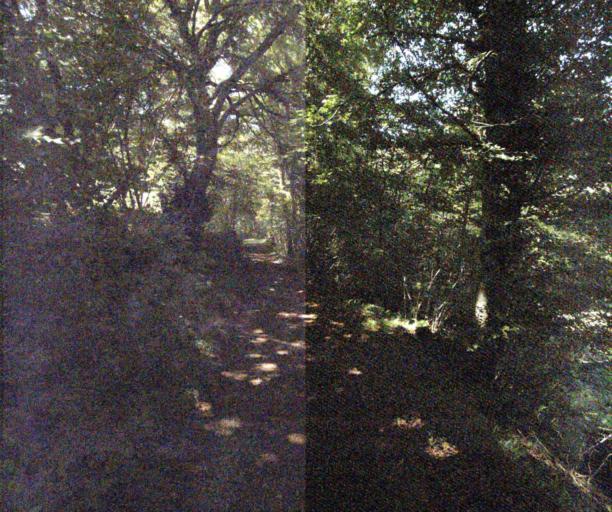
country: FR
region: Midi-Pyrenees
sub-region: Departement du Tarn
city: Dourgne
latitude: 43.4318
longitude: 2.1635
